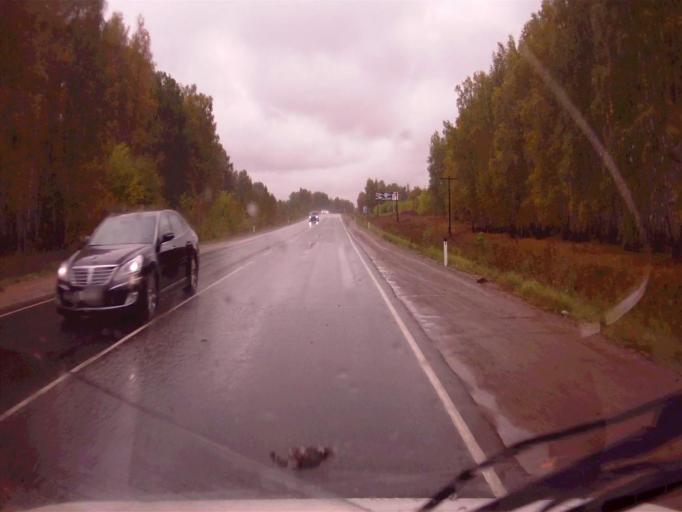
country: RU
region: Chelyabinsk
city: Argayash
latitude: 55.4678
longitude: 60.9077
